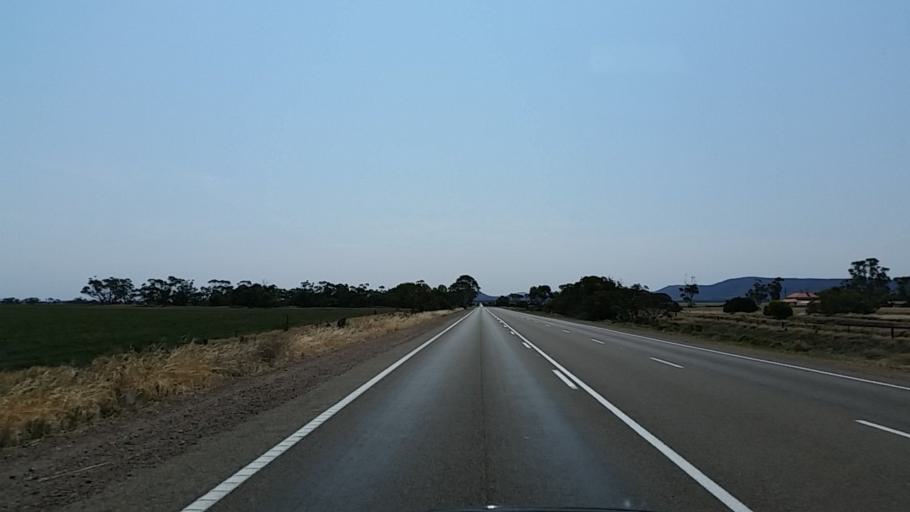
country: AU
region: South Australia
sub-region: Port Pirie City and Dists
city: Port Pirie
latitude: -32.9080
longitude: 137.9823
